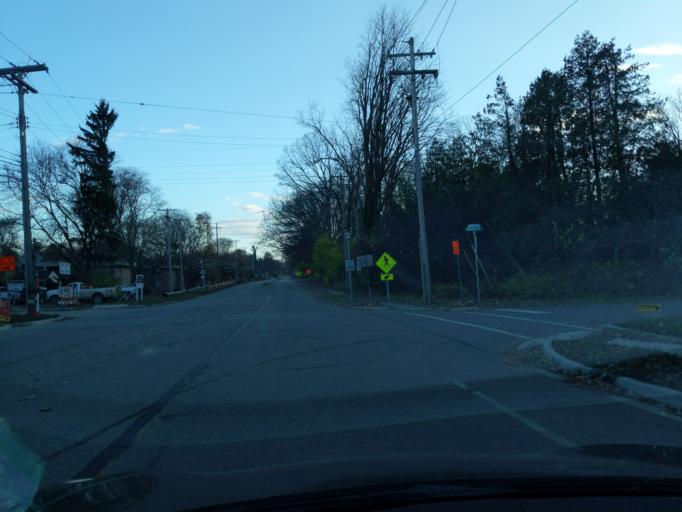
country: US
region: Michigan
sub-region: Ingham County
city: East Lansing
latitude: 42.7488
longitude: -84.4937
